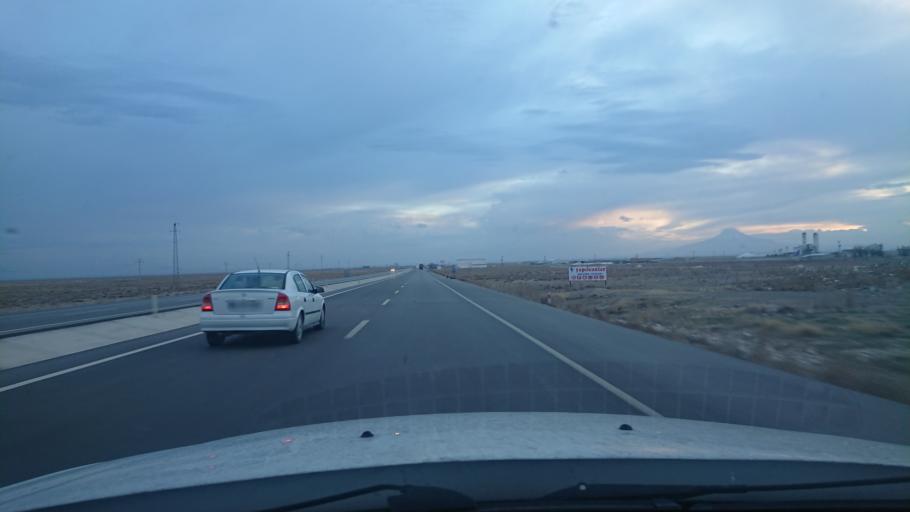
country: TR
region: Aksaray
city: Sultanhani
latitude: 38.2529
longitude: 33.5764
